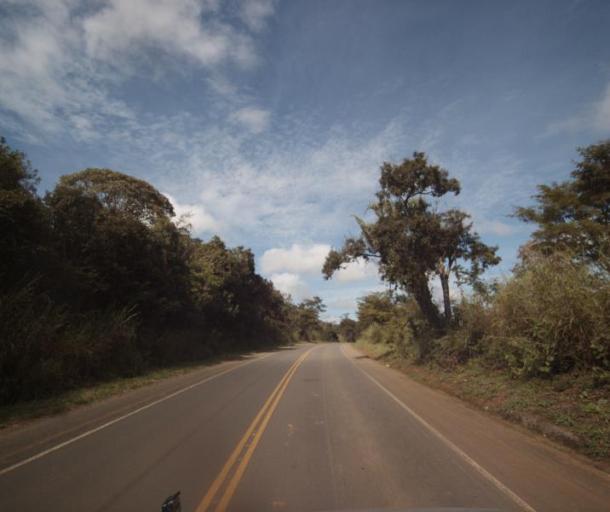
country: BR
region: Goias
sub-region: Pirenopolis
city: Pirenopolis
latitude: -15.9858
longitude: -48.8297
